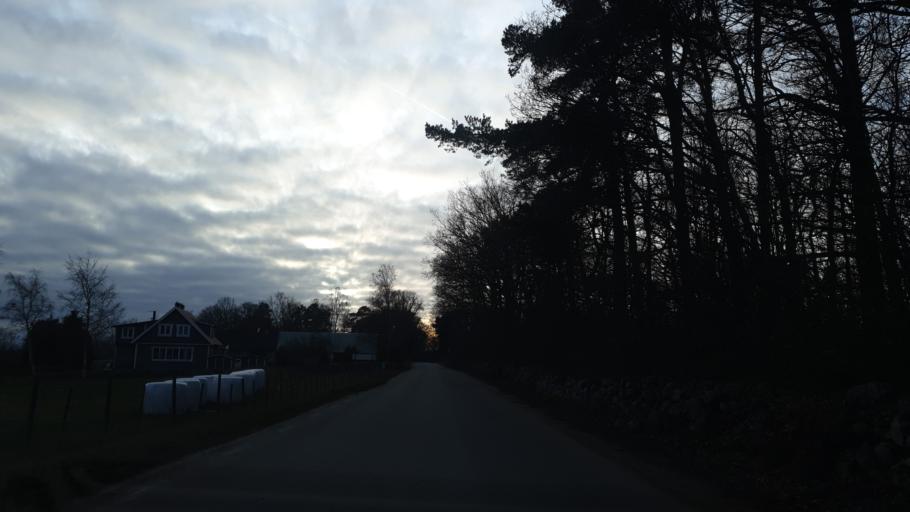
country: SE
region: Blekinge
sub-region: Karlskrona Kommun
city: Jaemjoe
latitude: 56.1614
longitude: 15.9166
